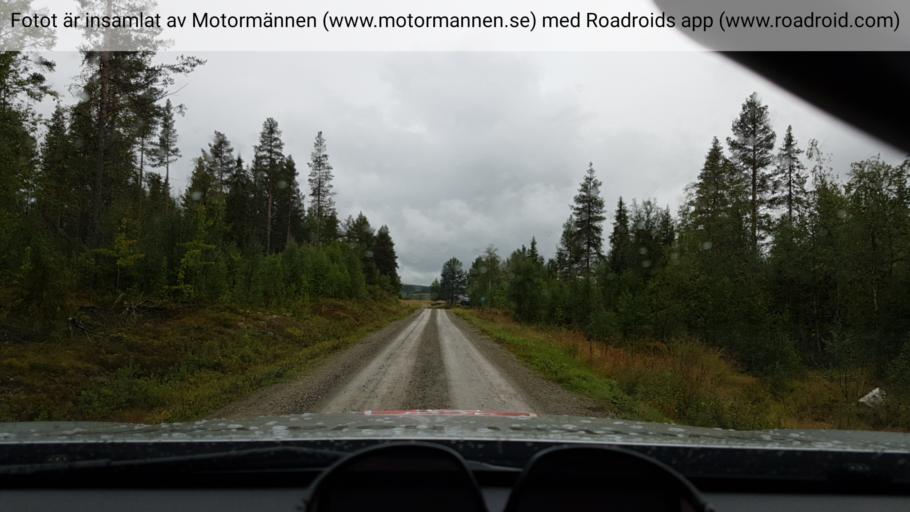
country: SE
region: Vaesterbotten
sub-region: Storumans Kommun
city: Storuman
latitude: 64.8247
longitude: 17.4099
